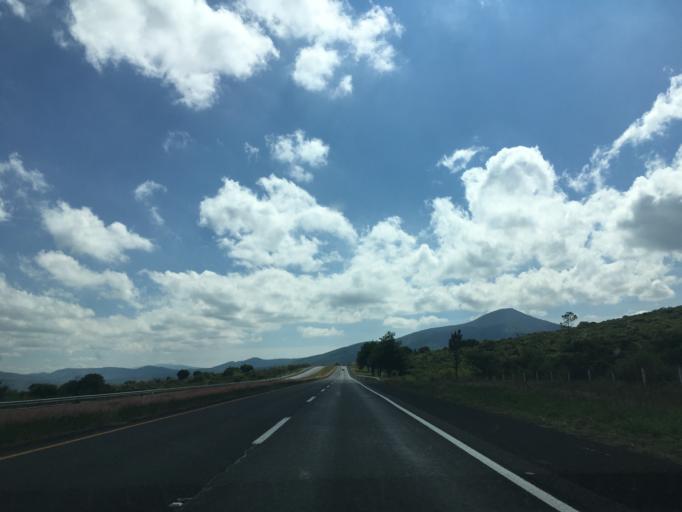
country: MX
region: Michoacan
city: Panindicuaro de la Reforma
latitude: 19.9792
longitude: -101.7803
